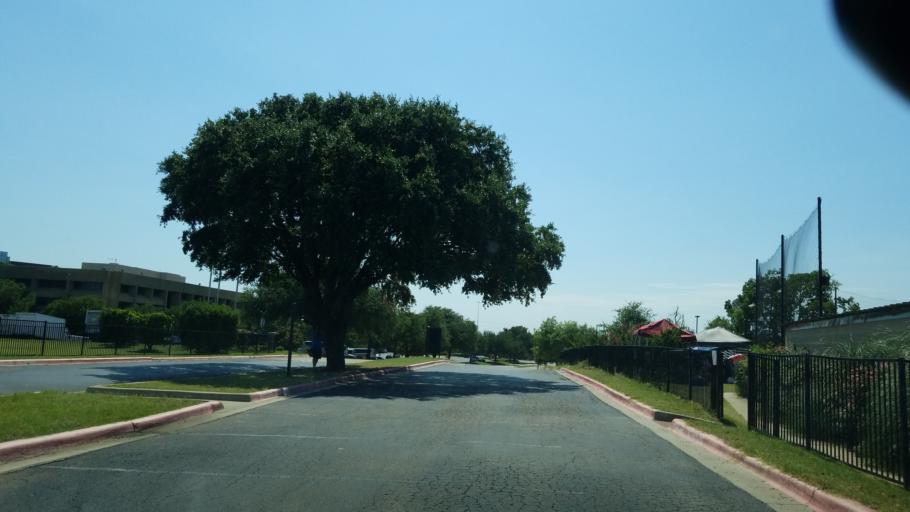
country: US
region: Texas
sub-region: Dallas County
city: Farmers Branch
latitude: 32.9145
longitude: -96.8883
